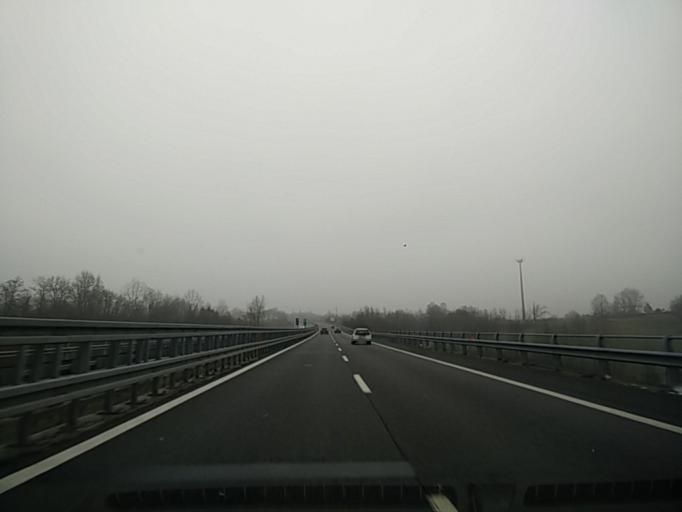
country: IT
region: Piedmont
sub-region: Provincia di Asti
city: Baldichieri d'Asti
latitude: 44.9024
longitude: 8.1174
